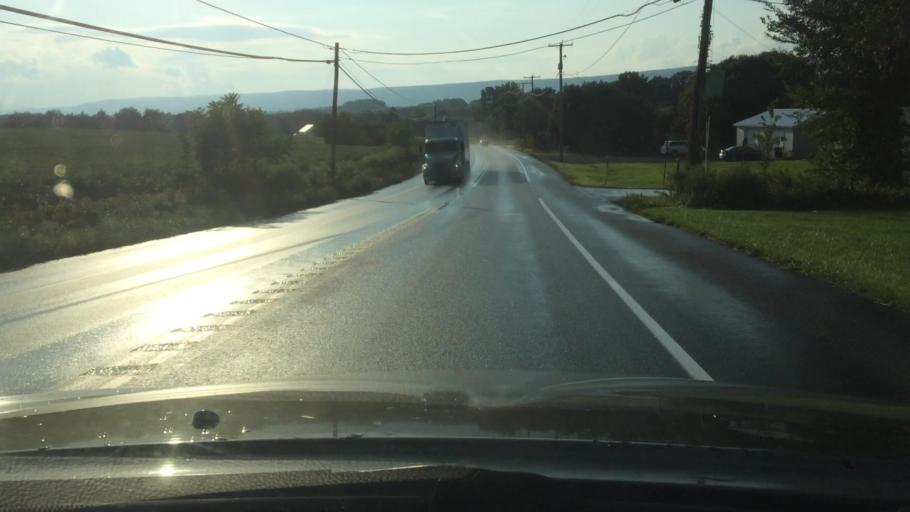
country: US
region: Pennsylvania
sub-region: Lehigh County
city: Schnecksville
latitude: 40.6821
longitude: -75.7336
